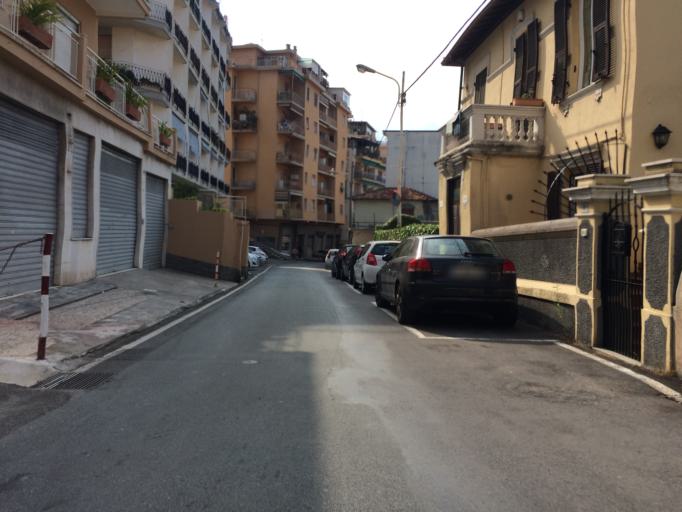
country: IT
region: Liguria
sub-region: Provincia di Imperia
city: San Remo
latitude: 43.8269
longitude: 7.7724
